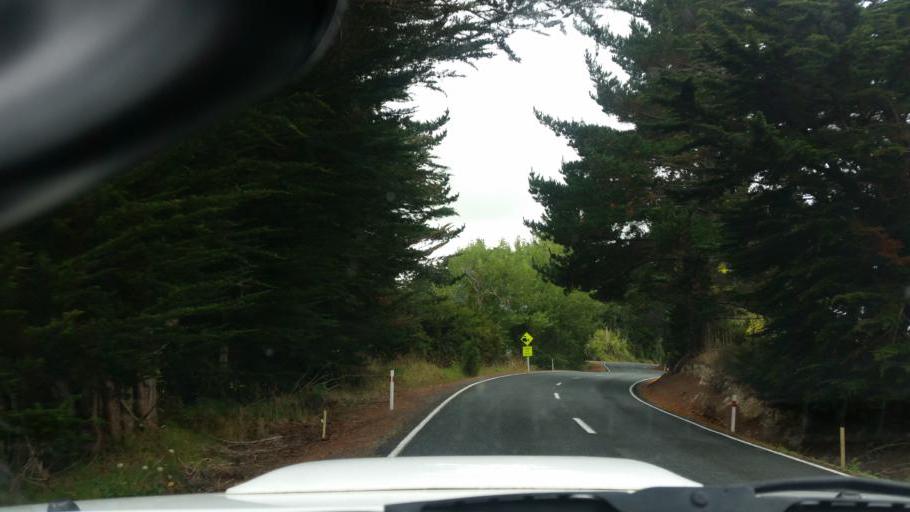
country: NZ
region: Auckland
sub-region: Auckland
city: Wellsford
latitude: -36.1449
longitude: 174.4827
